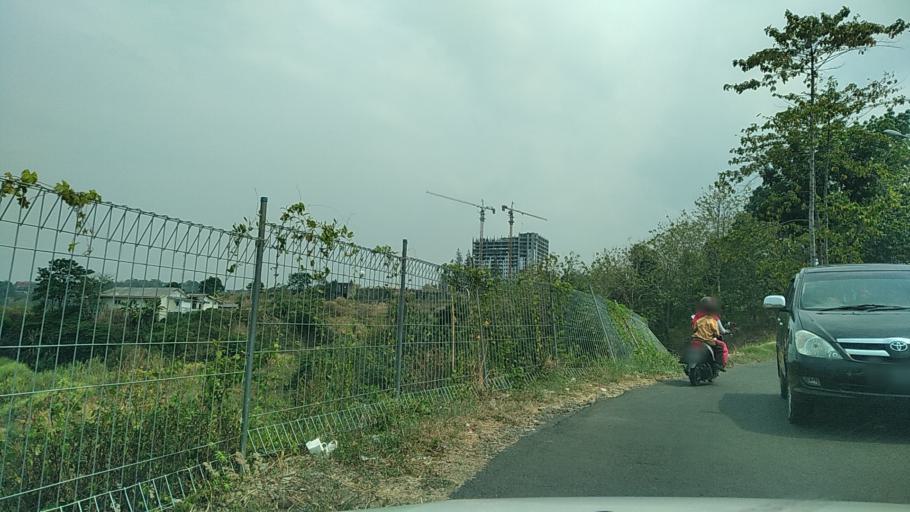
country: ID
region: Central Java
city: Semarang
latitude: -7.0006
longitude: 110.3287
